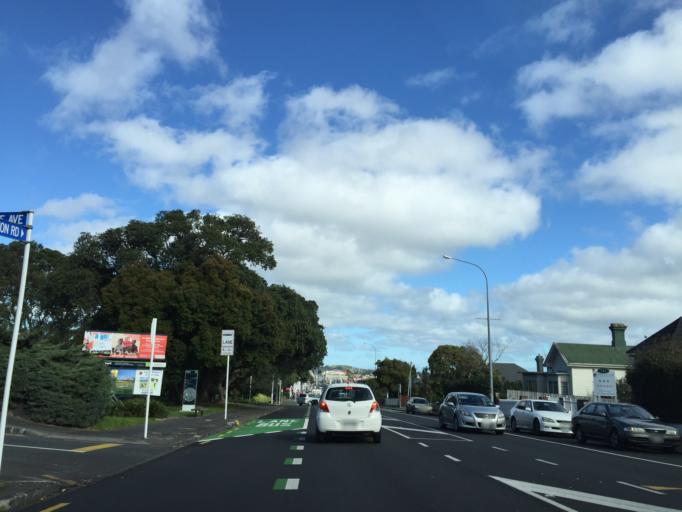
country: NZ
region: Auckland
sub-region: Auckland
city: Auckland
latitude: -36.8731
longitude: 174.7520
